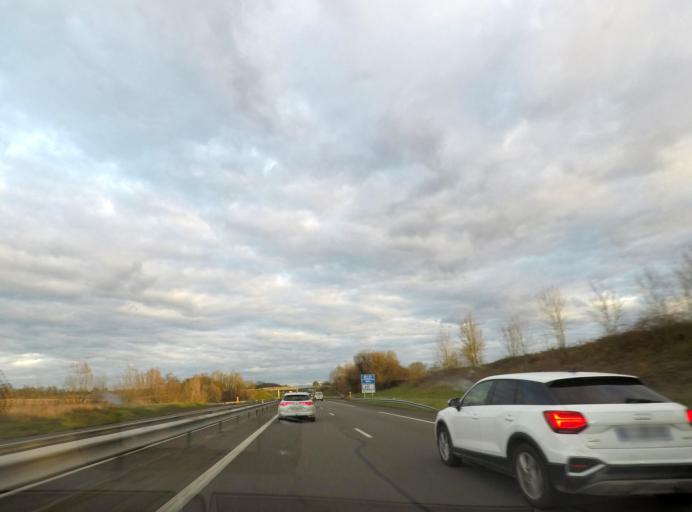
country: FR
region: Rhone-Alpes
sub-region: Departement de l'Ain
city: Saint-Cyr-sur-Menthon
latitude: 46.2804
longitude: 4.9738
